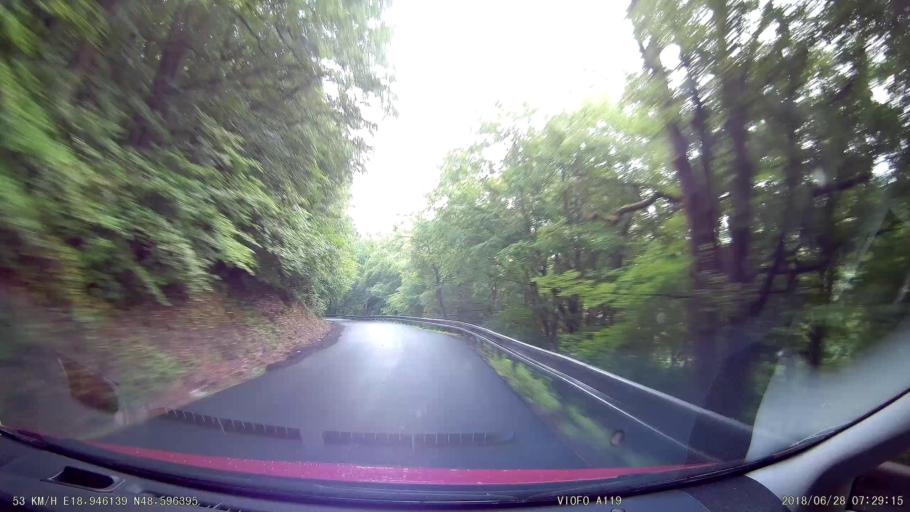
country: SK
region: Banskobystricky
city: Ziar nad Hronom
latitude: 48.5964
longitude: 18.9461
